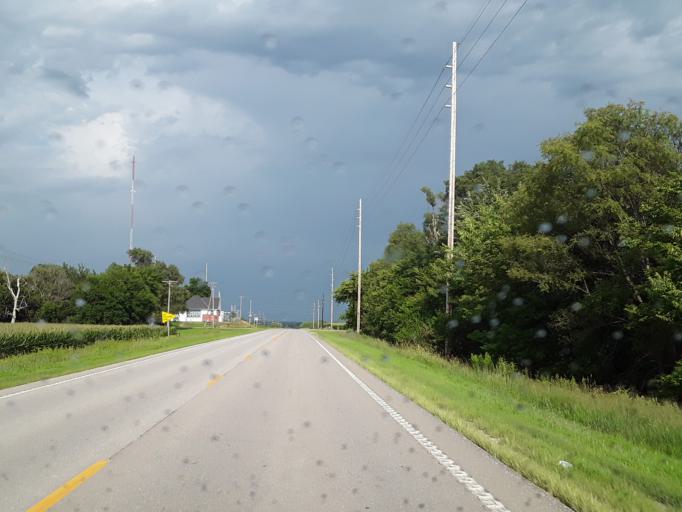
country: US
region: Nebraska
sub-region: Saunders County
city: Ashland
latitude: 41.0887
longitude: -96.3899
